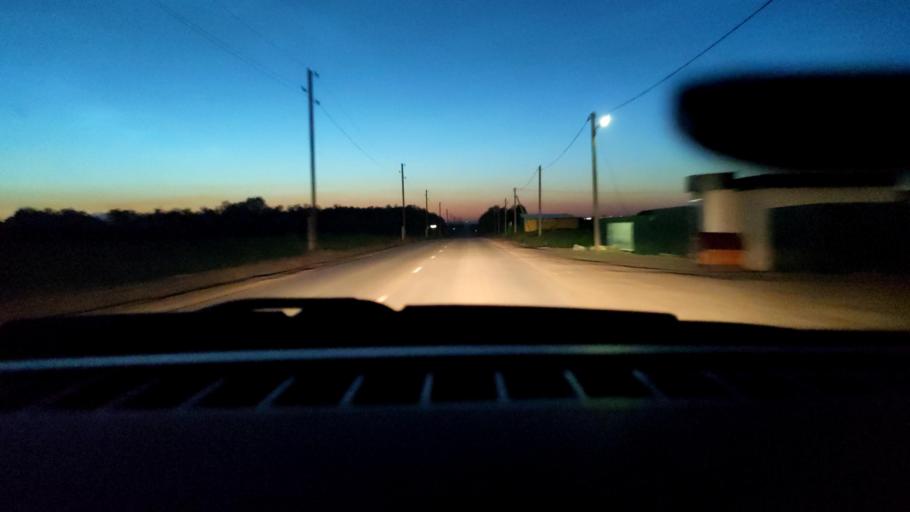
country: RU
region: Perm
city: Kultayevo
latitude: 57.8785
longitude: 55.9879
